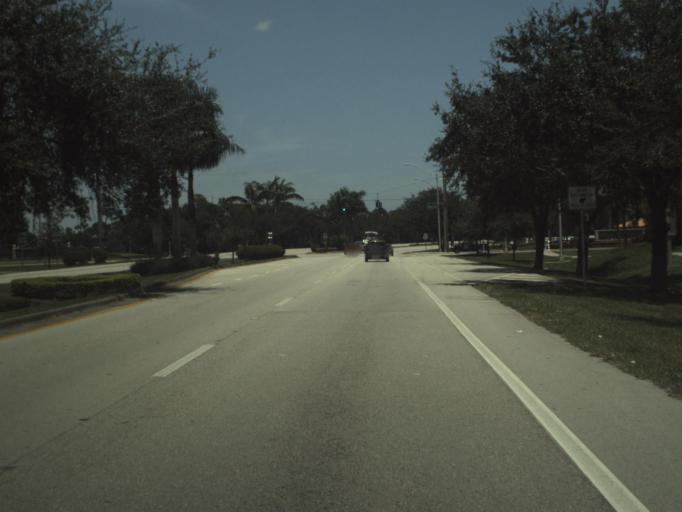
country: US
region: Florida
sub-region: Martin County
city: Palm City
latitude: 27.1693
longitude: -80.2986
